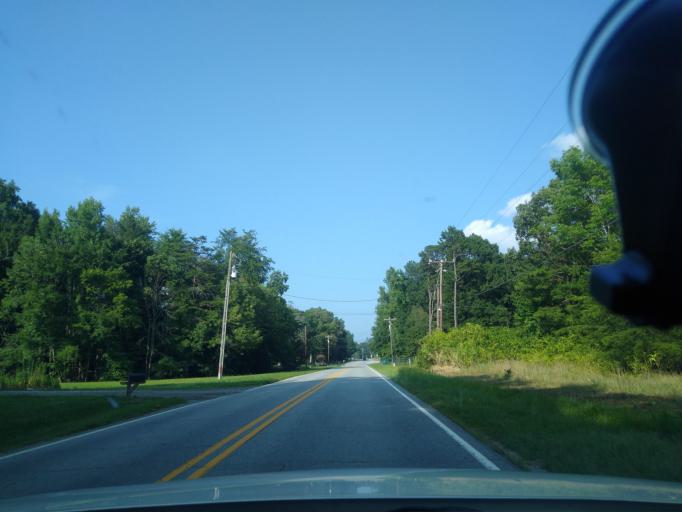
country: US
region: North Carolina
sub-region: Guilford County
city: McLeansville
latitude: 36.0969
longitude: -79.6711
